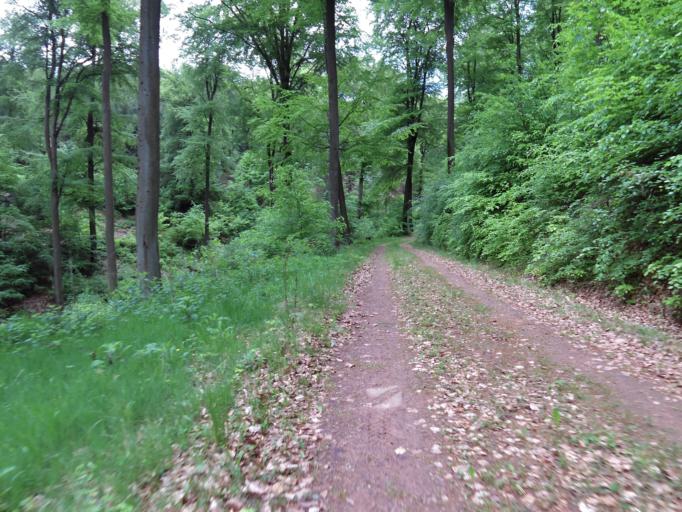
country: DE
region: Rheinland-Pfalz
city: Neidenfels
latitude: 49.4127
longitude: 8.0513
